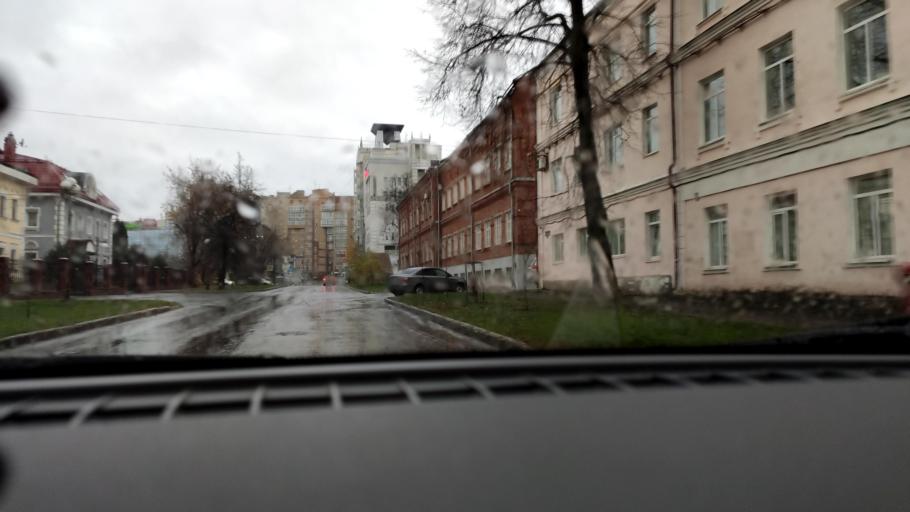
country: RU
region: Perm
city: Perm
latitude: 58.0179
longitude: 56.2570
